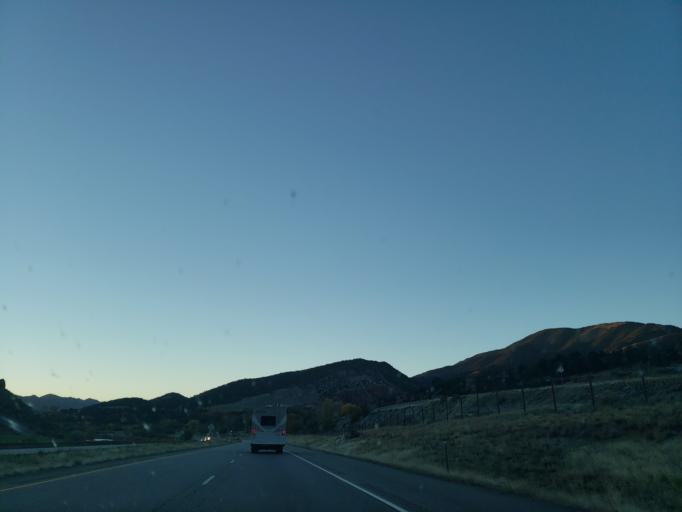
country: US
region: Colorado
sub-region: Garfield County
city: New Castle
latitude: 39.5715
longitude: -107.4614
